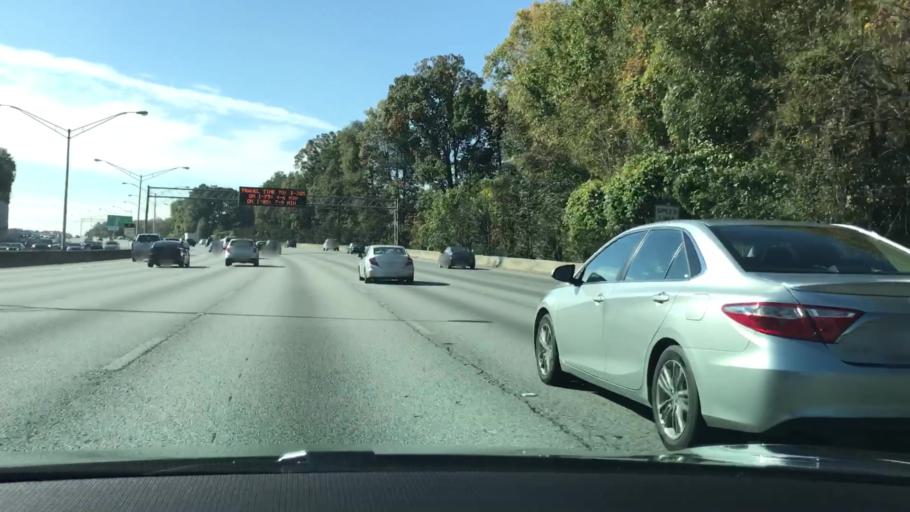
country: US
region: Georgia
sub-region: Fulton County
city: Atlanta
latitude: 33.7131
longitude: -84.4006
